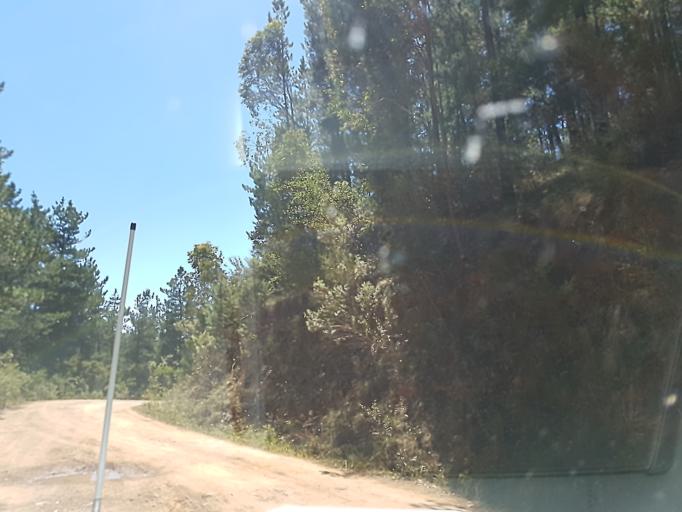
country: AU
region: Victoria
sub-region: Alpine
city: Mount Beauty
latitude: -36.7440
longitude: 146.9594
